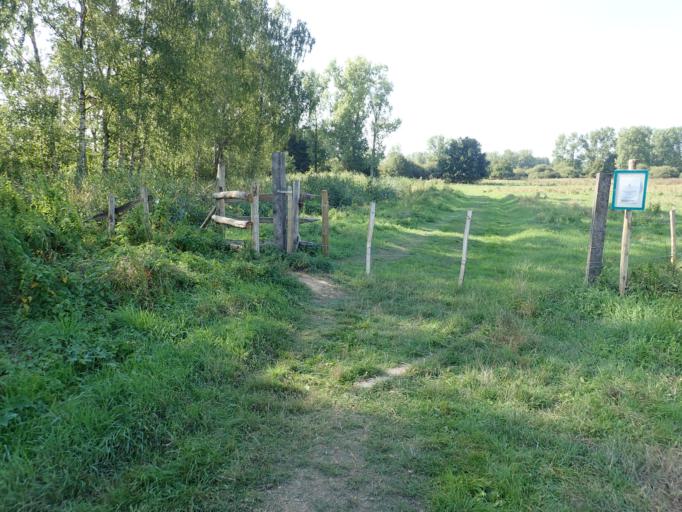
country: BE
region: Flanders
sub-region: Provincie Vlaams-Brabant
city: Scherpenheuvel-Zichem
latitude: 51.0103
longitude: 4.9776
